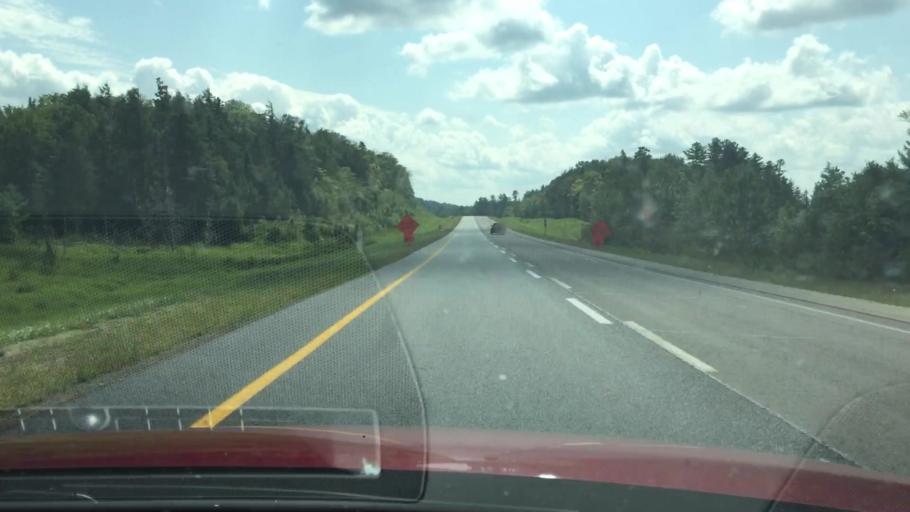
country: US
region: Maine
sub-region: Penobscot County
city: Medway
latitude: 45.7253
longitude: -68.4740
